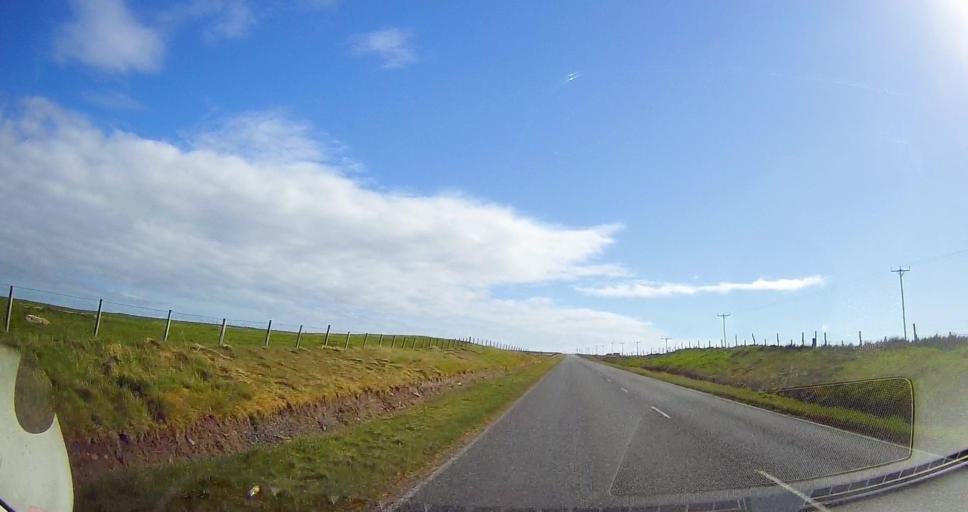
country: GB
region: Scotland
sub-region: Shetland Islands
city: Sandwick
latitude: 59.9051
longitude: -1.3025
